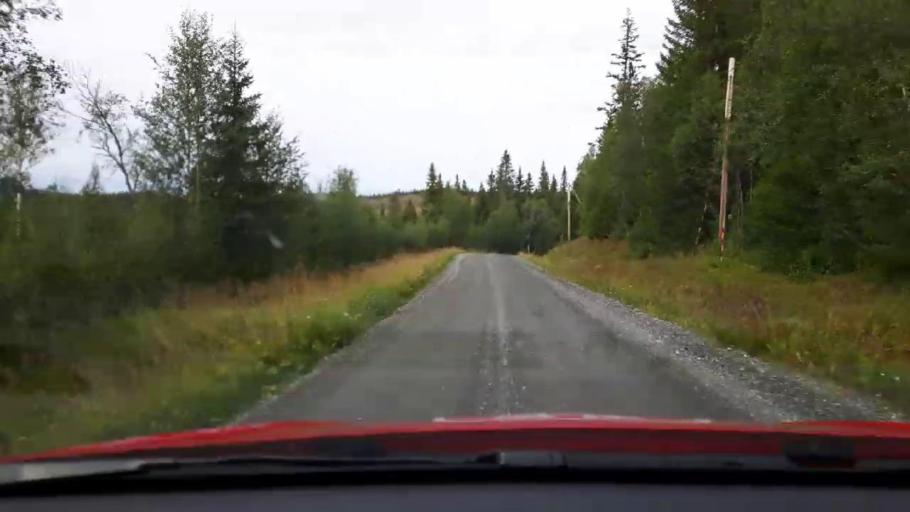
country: SE
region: Jaemtland
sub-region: Are Kommun
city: Are
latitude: 63.7683
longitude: 13.0927
